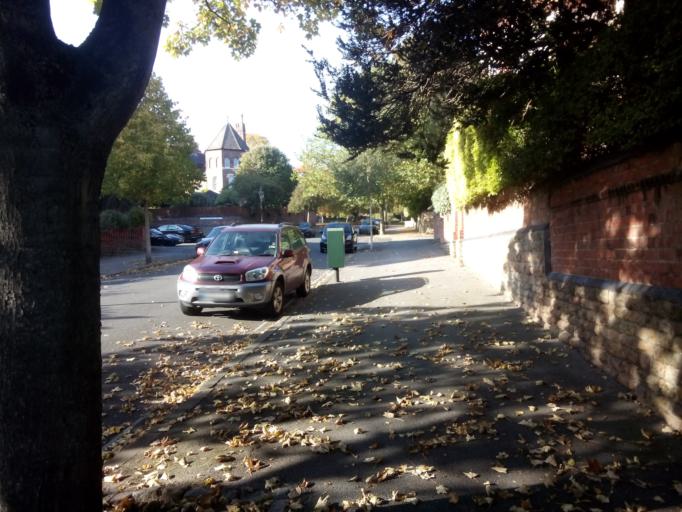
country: GB
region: England
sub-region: Nottingham
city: Nottingham
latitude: 52.9494
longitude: -1.1629
